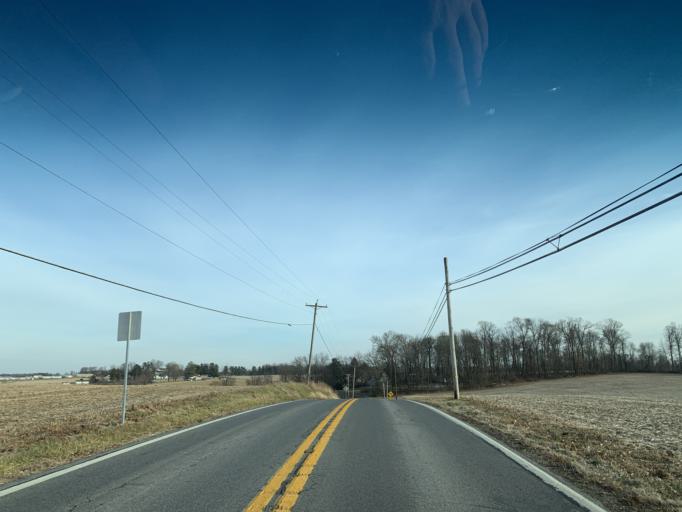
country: US
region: Maryland
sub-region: Carroll County
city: Hampstead
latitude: 39.6022
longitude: -76.7896
